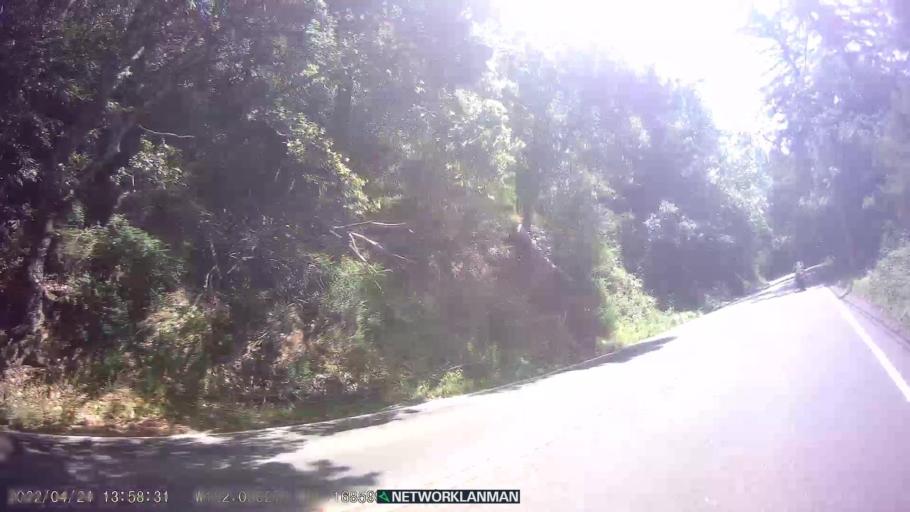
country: US
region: California
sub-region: Santa Cruz County
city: Lompico
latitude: 37.1684
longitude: -122.0501
